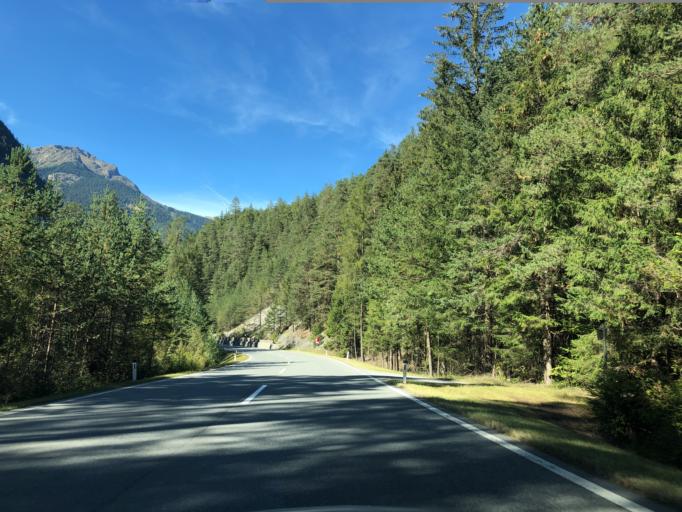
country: AT
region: Tyrol
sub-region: Politischer Bezirk Imst
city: Umhausen
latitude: 47.1245
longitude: 10.9288
